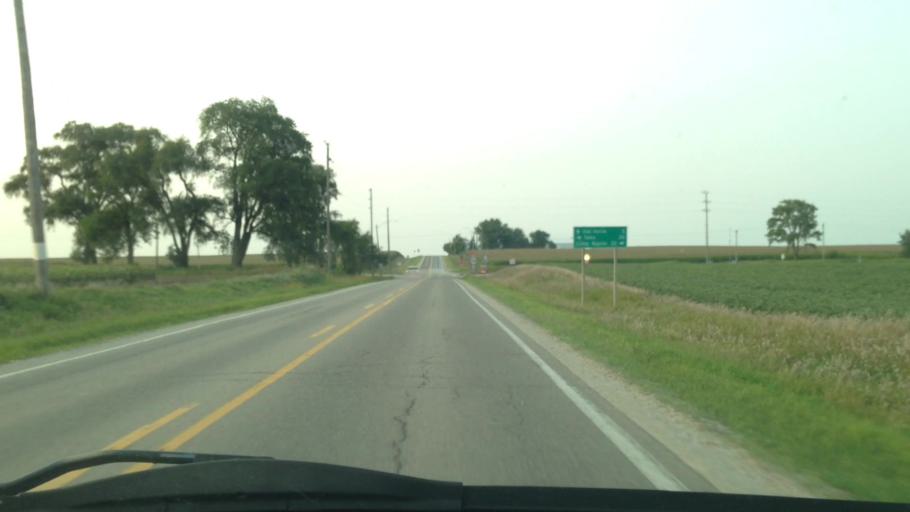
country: US
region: Iowa
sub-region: Iowa County
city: Marengo
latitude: 41.9619
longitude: -92.0853
